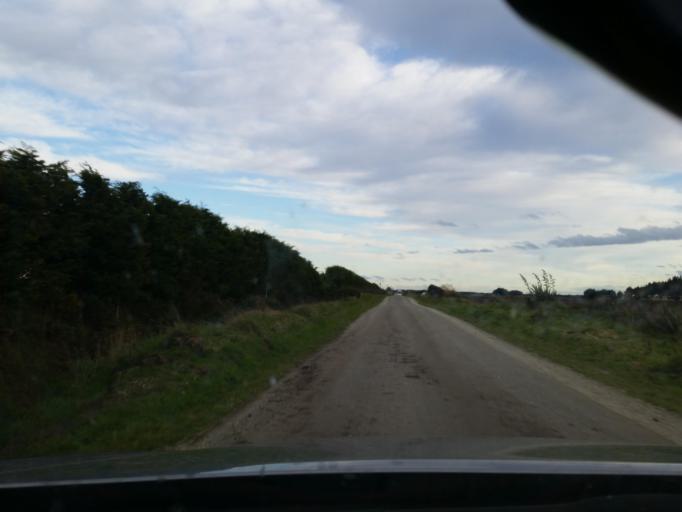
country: NZ
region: Southland
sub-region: Invercargill City
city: Invercargill
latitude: -46.4383
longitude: 168.5062
